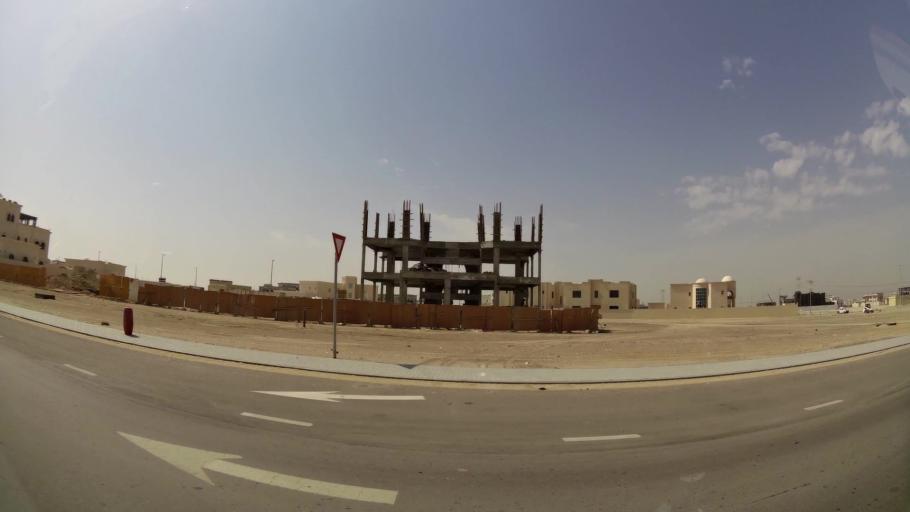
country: AE
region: Abu Dhabi
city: Abu Dhabi
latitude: 24.3004
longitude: 54.5753
